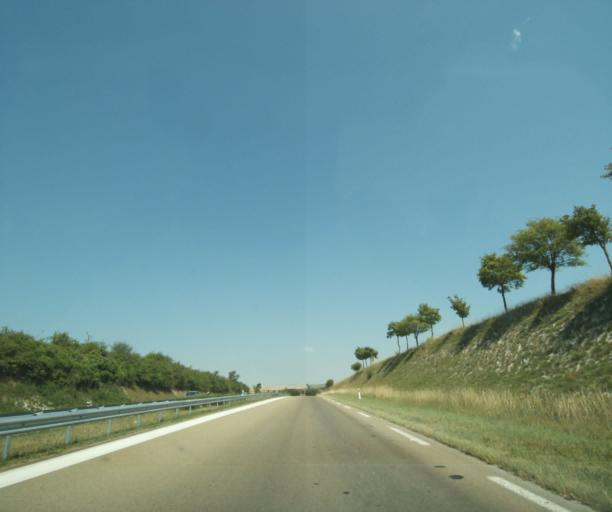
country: FR
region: Champagne-Ardenne
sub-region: Departement de la Marne
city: Fagnieres
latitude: 49.0534
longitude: 4.3019
